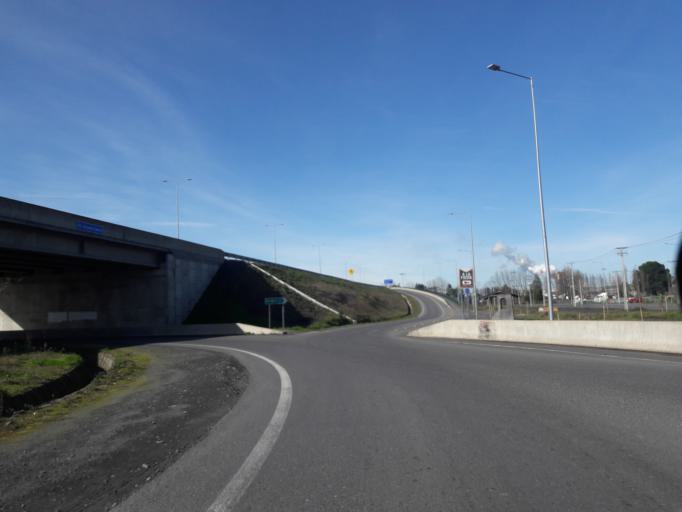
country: CL
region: Biobio
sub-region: Provincia de Biobio
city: Cabrero
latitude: -37.0397
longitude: -72.4056
